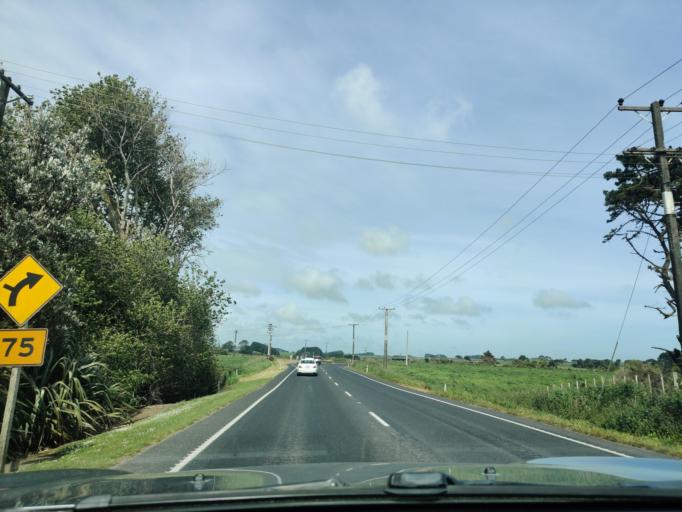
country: NZ
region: Taranaki
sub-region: South Taranaki District
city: Hawera
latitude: -39.6301
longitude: 174.3755
